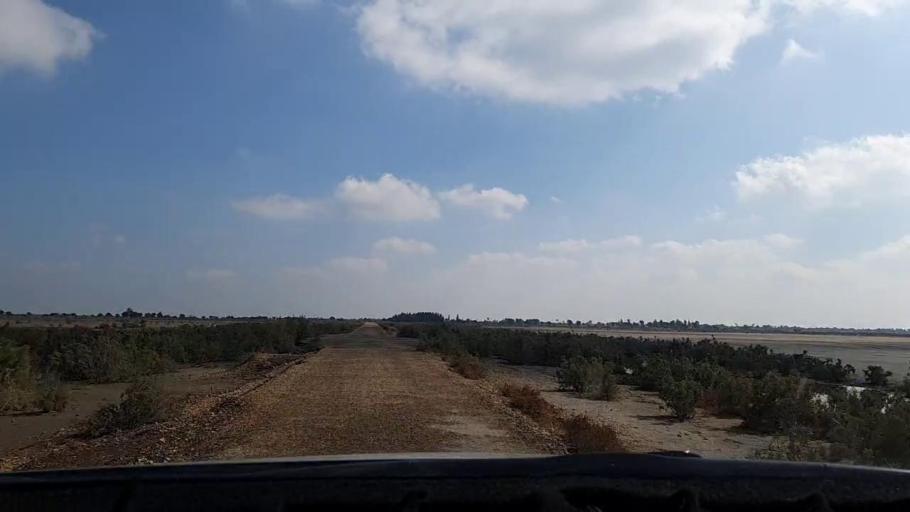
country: PK
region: Sindh
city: Pithoro
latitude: 25.7342
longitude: 69.2811
